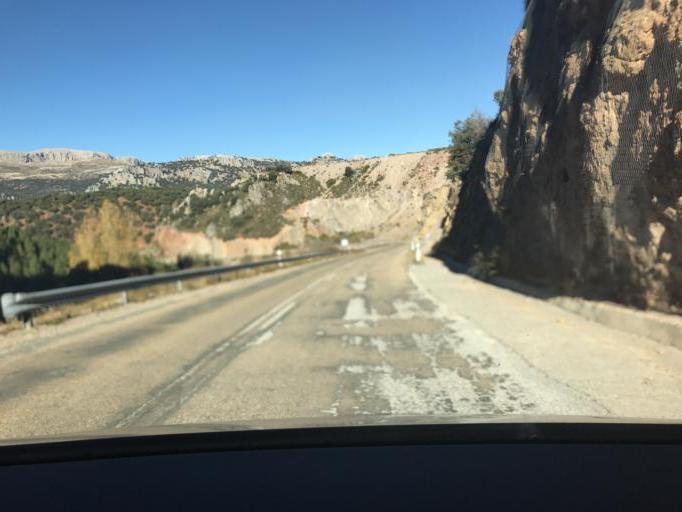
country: ES
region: Andalusia
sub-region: Provincia de Granada
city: Beas de Granada
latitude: 37.2967
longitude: -3.4505
